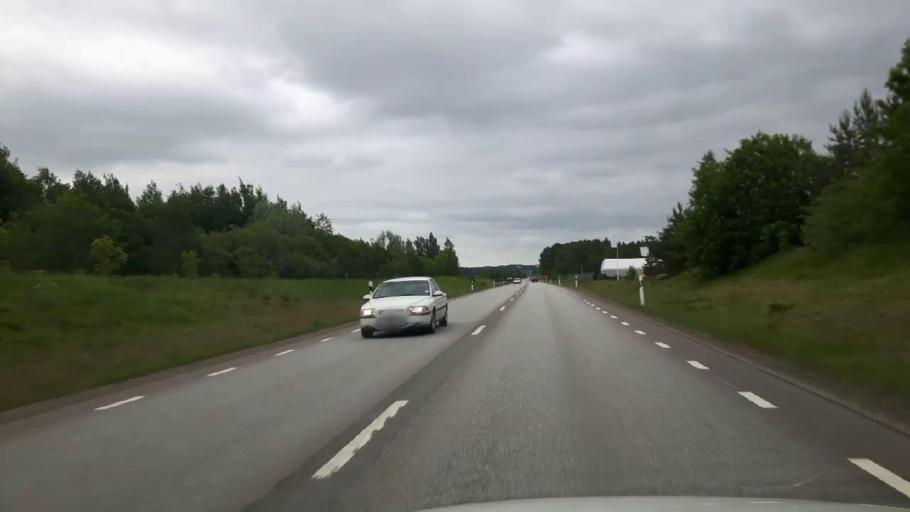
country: SE
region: Vaestmanland
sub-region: Kopings Kommun
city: Koping
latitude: 59.5413
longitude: 15.9380
